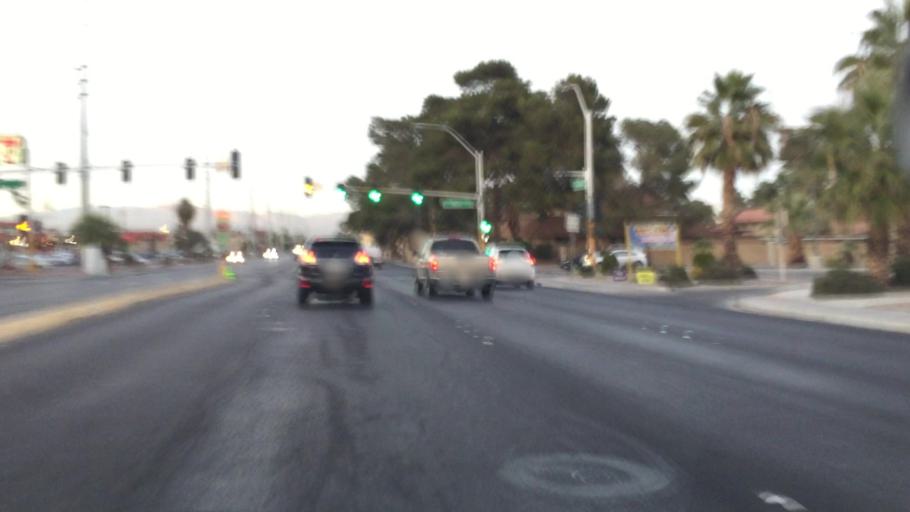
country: US
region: Nevada
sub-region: Clark County
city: Paradise
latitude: 36.0960
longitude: -115.1189
